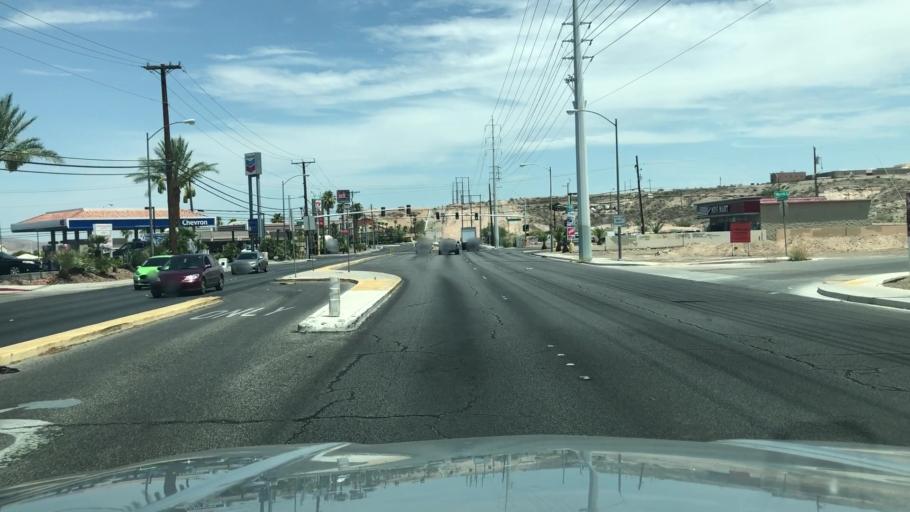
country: US
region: Nevada
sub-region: Clark County
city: Whitney
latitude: 36.0856
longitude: -115.0746
